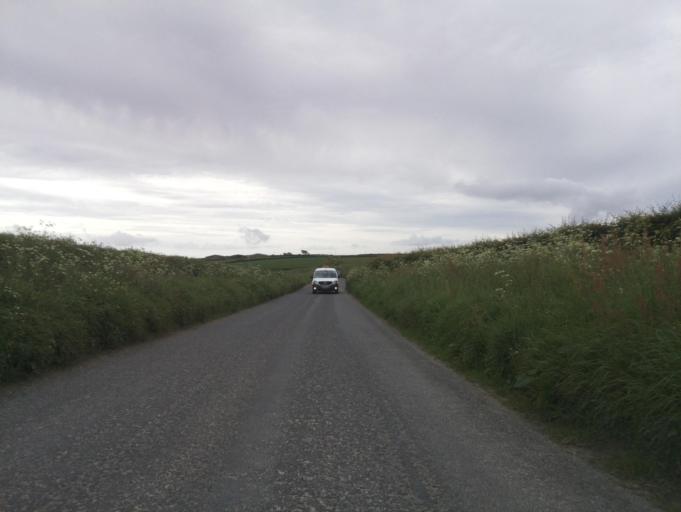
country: GB
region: England
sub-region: Devon
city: Dartmouth
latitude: 50.3254
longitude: -3.6399
